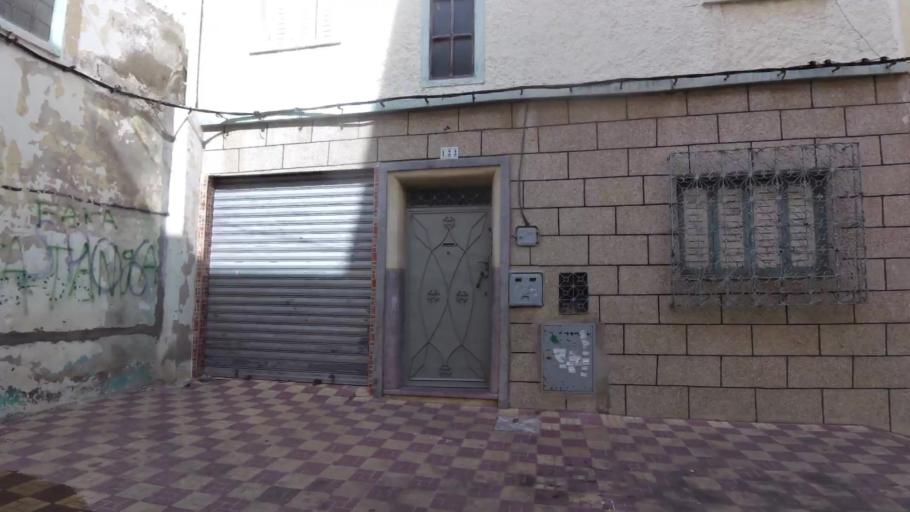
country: MA
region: Tanger-Tetouan
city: Tetouan
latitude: 35.5837
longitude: -5.3515
